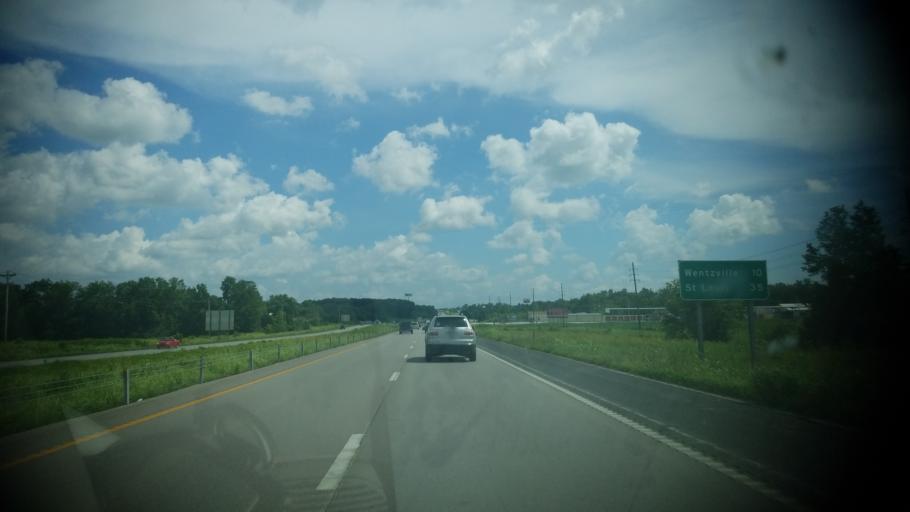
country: US
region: Missouri
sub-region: Lincoln County
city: Moscow Mills
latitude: 38.9349
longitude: -90.9257
